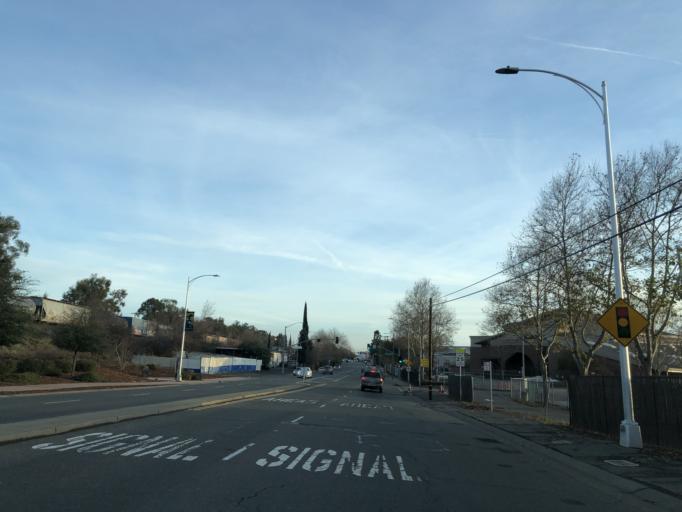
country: US
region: California
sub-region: Sacramento County
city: Arden-Arcade
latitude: 38.5615
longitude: -121.4308
